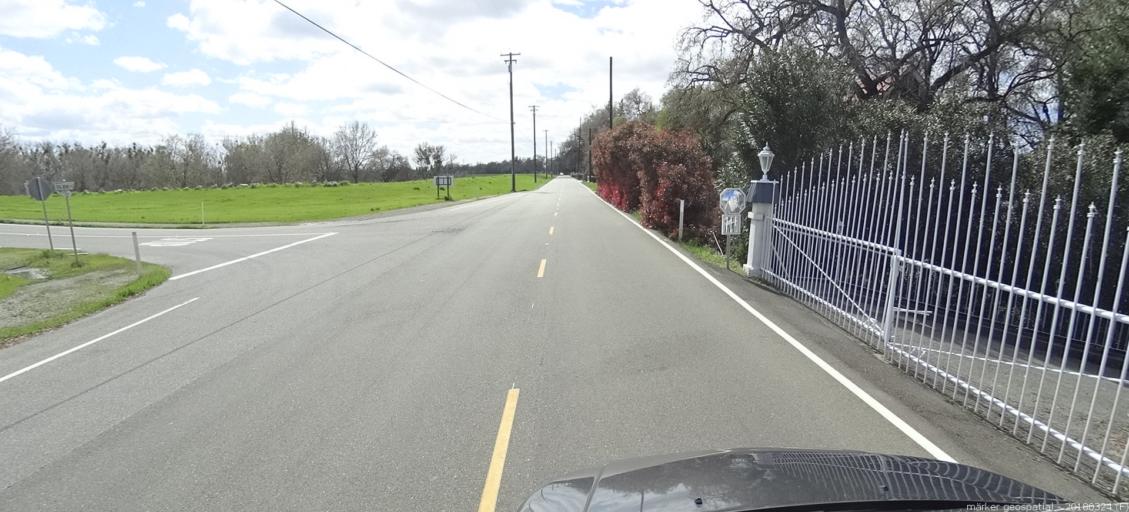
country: US
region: California
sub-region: Yolo County
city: Woodland
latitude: 38.7012
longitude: -121.6231
